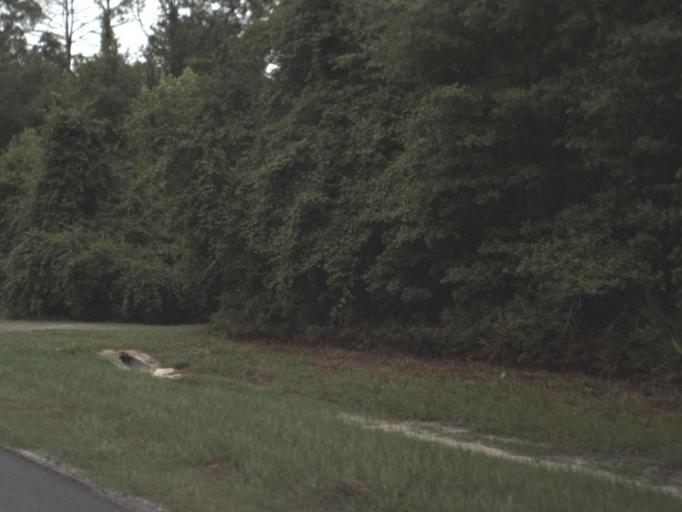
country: US
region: Florida
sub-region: Columbia County
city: Five Points
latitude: 30.4409
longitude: -82.6455
